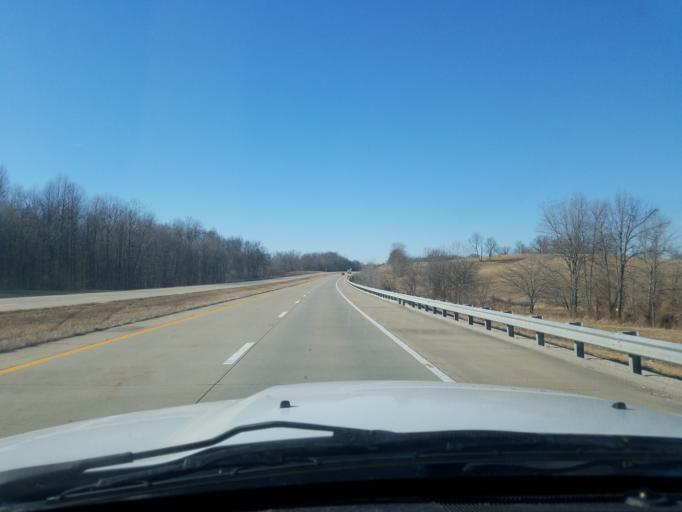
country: US
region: Indiana
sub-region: Warrick County
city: Newburgh
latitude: 37.7556
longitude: -87.4074
